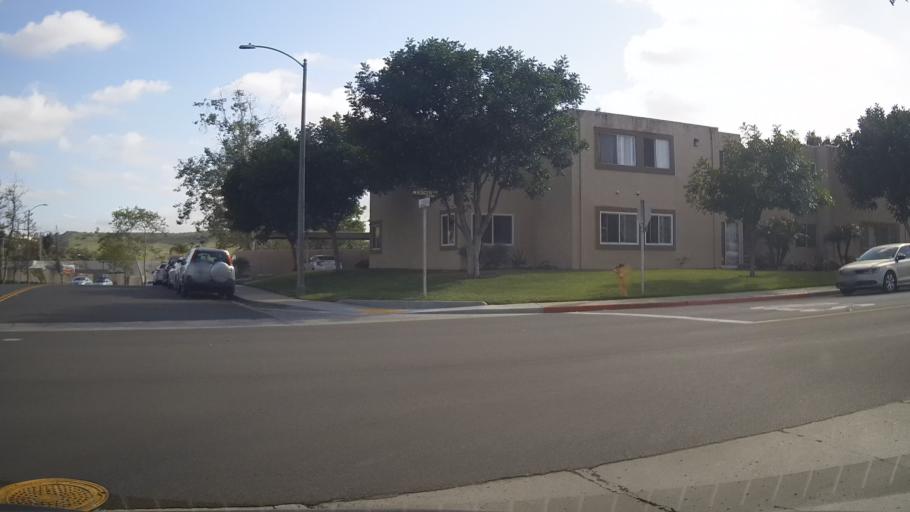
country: US
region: California
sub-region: San Diego County
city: Poway
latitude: 32.9573
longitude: -117.0562
